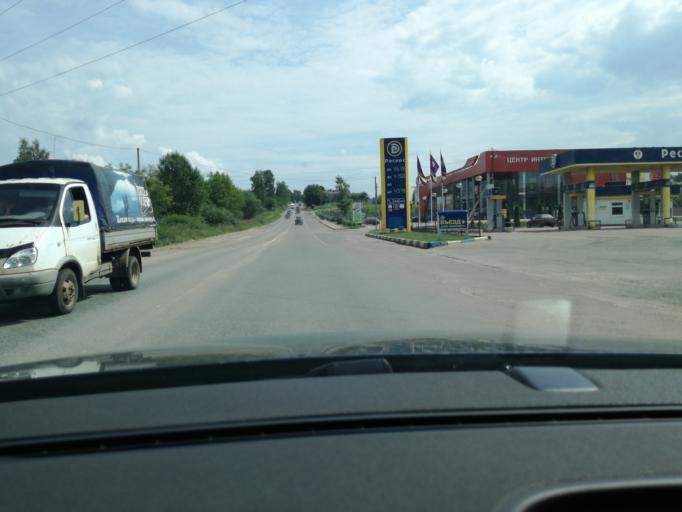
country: RU
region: Moskovskaya
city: Dmitrov
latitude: 56.3367
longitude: 37.5548
